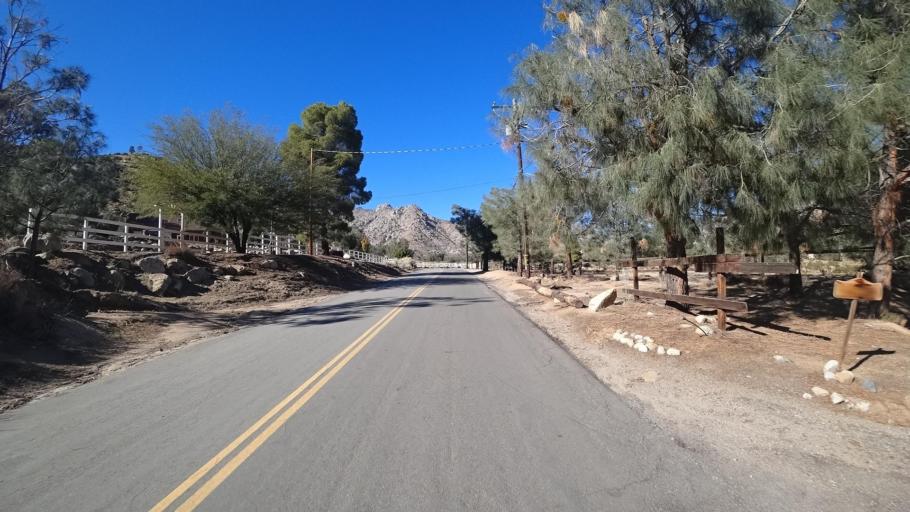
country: US
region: California
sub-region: Kern County
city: Kernville
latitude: 35.7755
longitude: -118.4446
